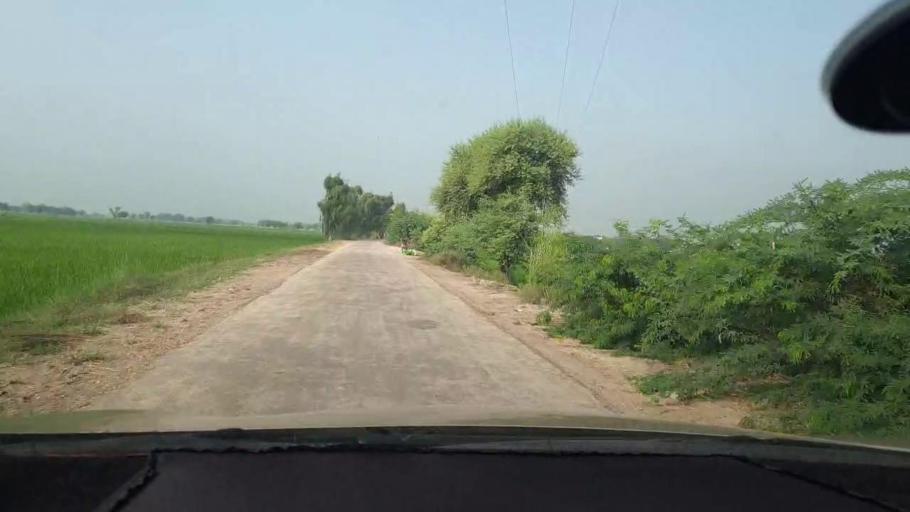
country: PK
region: Sindh
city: Goth Garelo
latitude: 27.4789
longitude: 68.0136
